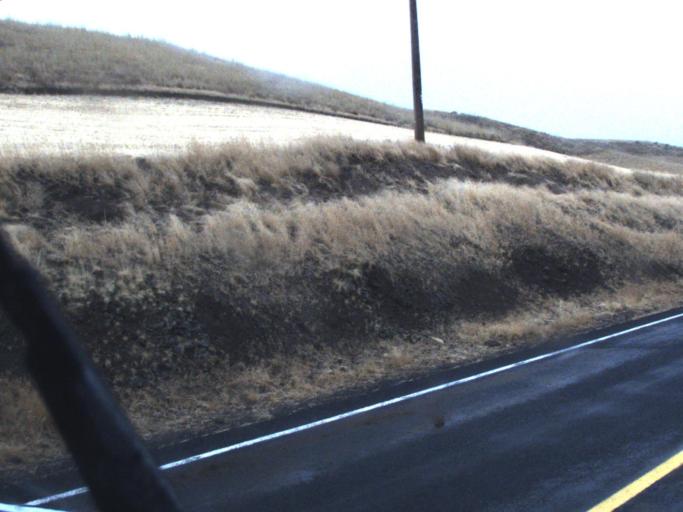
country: US
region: Washington
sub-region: Spokane County
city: Cheney
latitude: 47.1179
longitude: -117.8244
